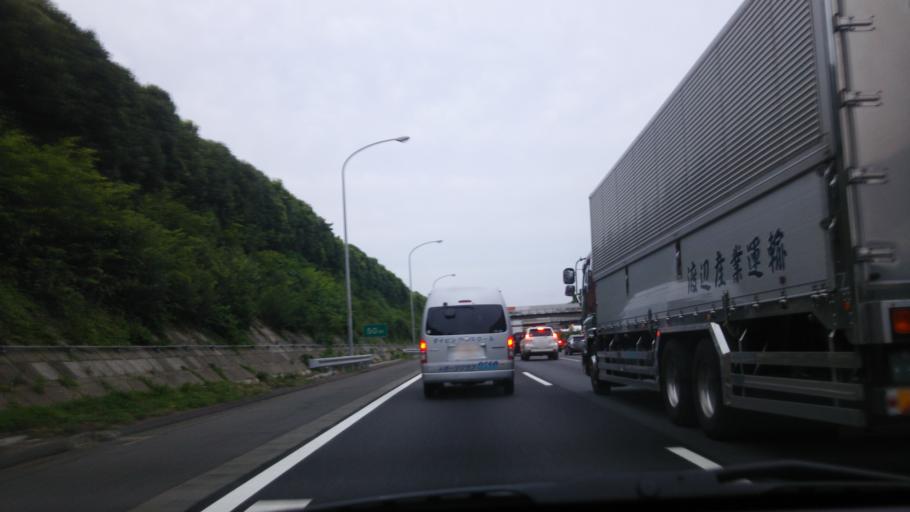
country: JP
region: Kanagawa
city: Minami-rinkan
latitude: 35.4590
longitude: 139.4303
